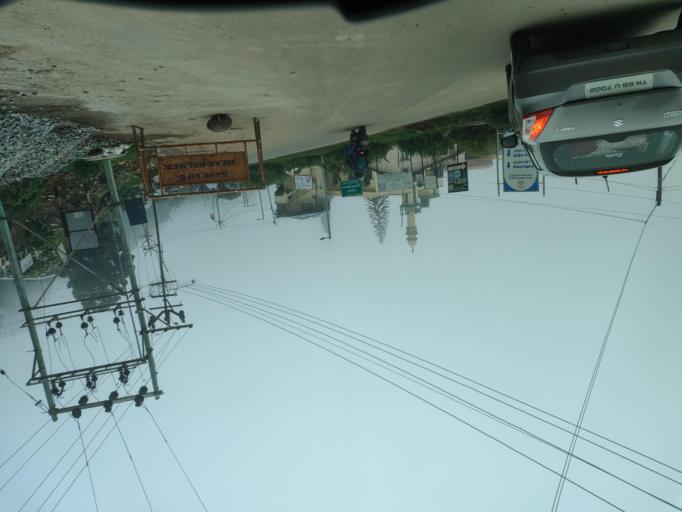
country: IN
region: Tamil Nadu
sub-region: Dindigul
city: Kodaikanal
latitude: 10.2312
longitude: 77.4730
